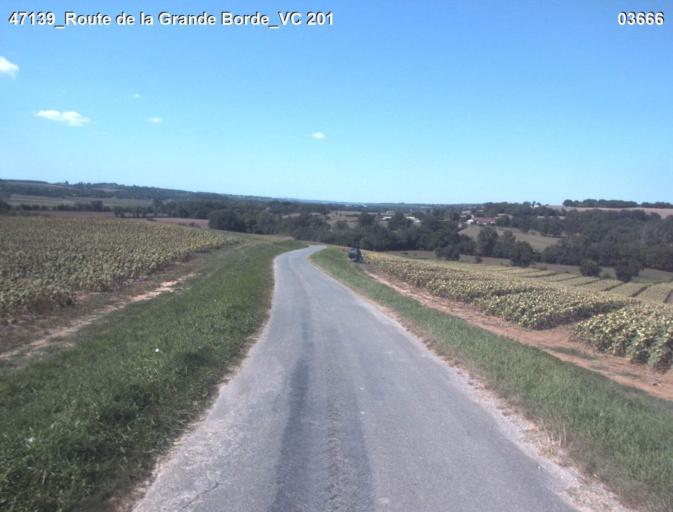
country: FR
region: Aquitaine
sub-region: Departement du Lot-et-Garonne
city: Nerac
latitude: 44.0910
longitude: 0.3784
